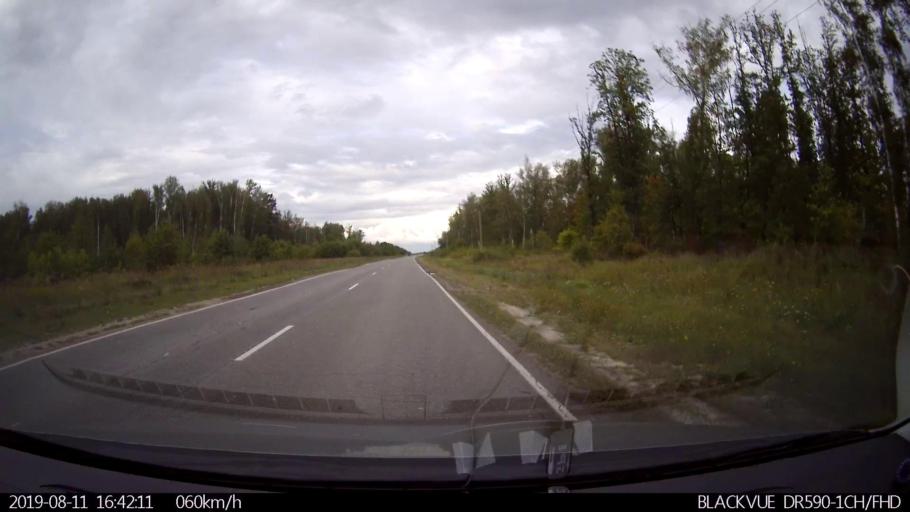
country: RU
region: Ulyanovsk
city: Mayna
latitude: 54.1585
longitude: 47.6601
